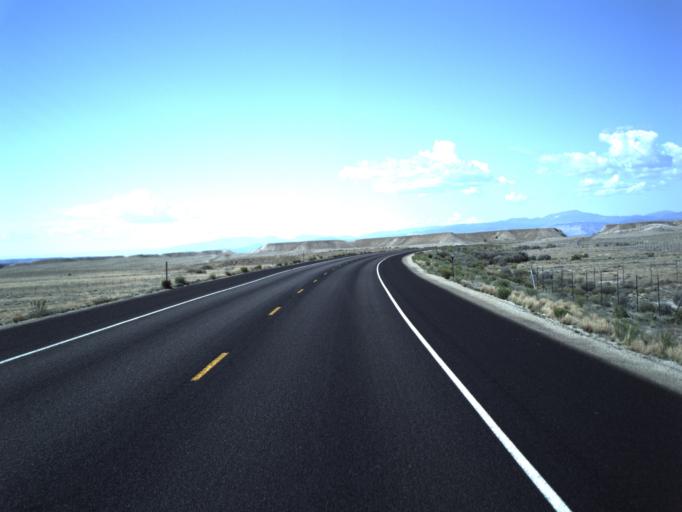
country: US
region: Utah
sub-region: Emery County
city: Ferron
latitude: 38.9755
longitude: -111.1773
